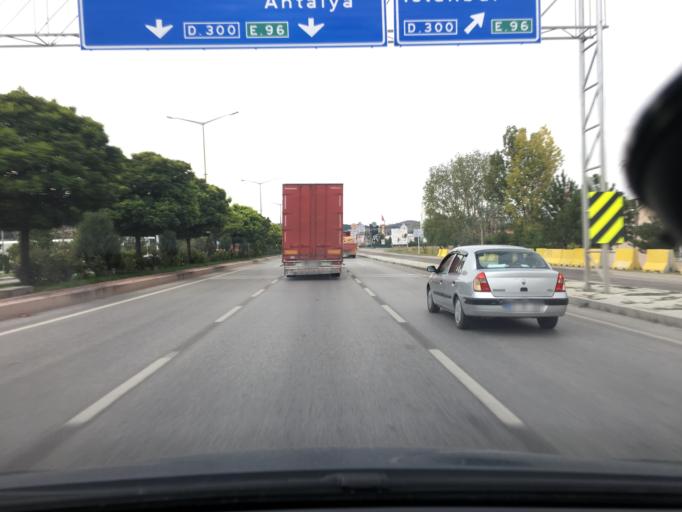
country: TR
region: Afyonkarahisar
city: Afyonkarahisar
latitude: 38.7883
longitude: 30.4632
